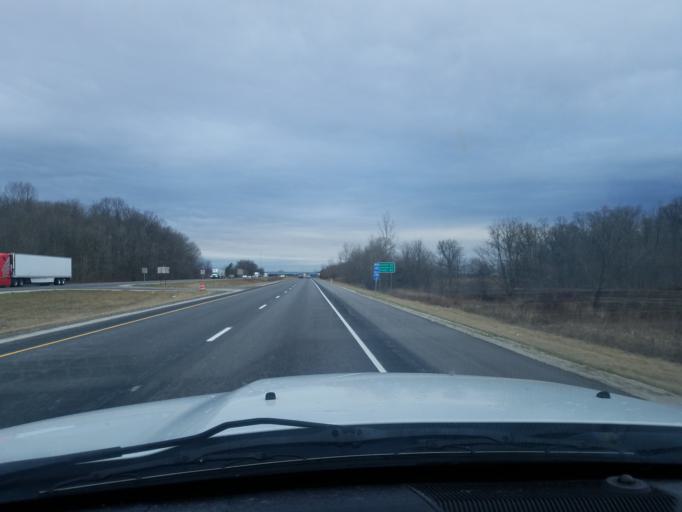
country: US
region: Indiana
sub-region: Boone County
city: Thorntown
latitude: 40.1355
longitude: -86.5214
